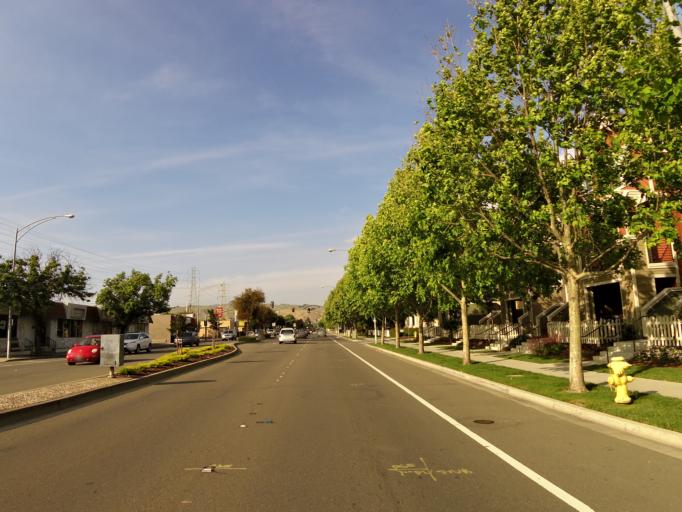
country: US
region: California
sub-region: Alameda County
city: Fremont
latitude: 37.5325
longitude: -121.9686
